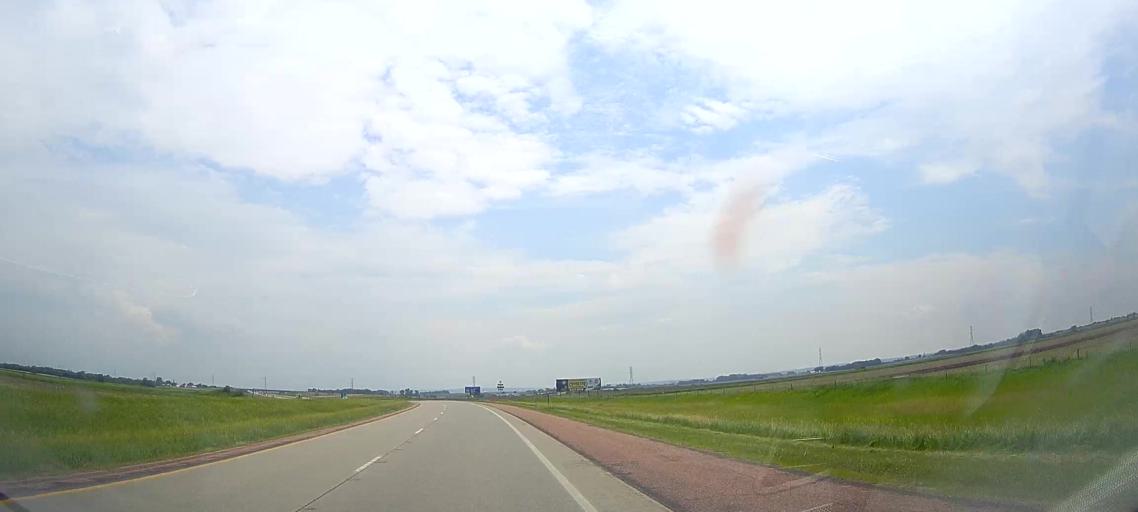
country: US
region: South Dakota
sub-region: Clay County
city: Vermillion
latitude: 42.7950
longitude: -96.7961
